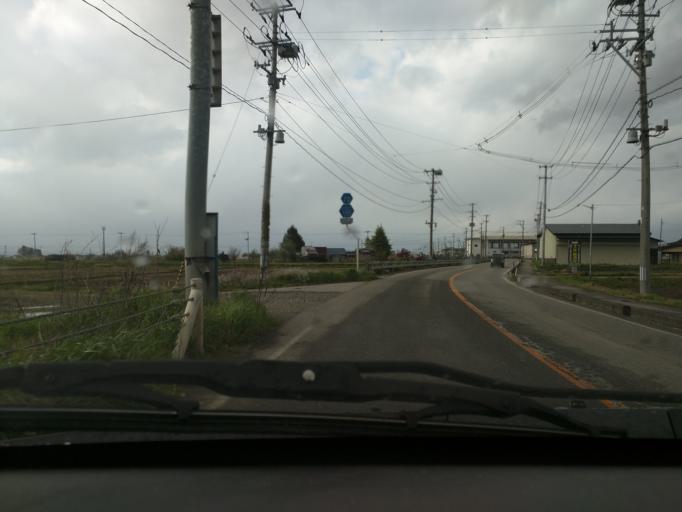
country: JP
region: Fukushima
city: Kitakata
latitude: 37.4492
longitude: 139.8810
